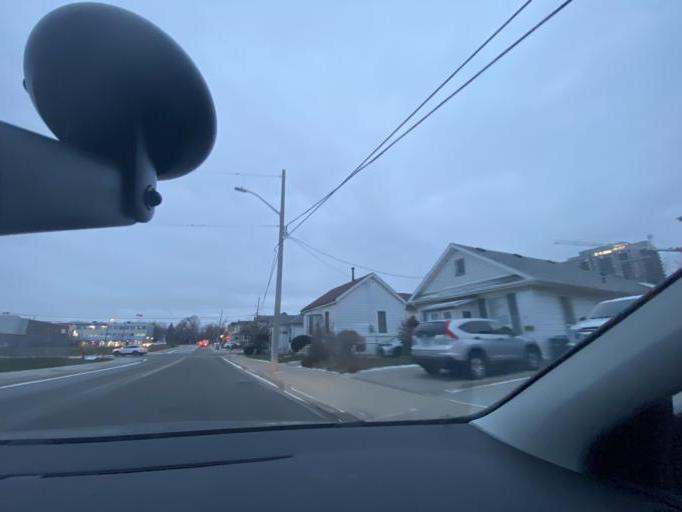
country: CA
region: Ontario
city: Brampton
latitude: 43.6920
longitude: -79.7510
